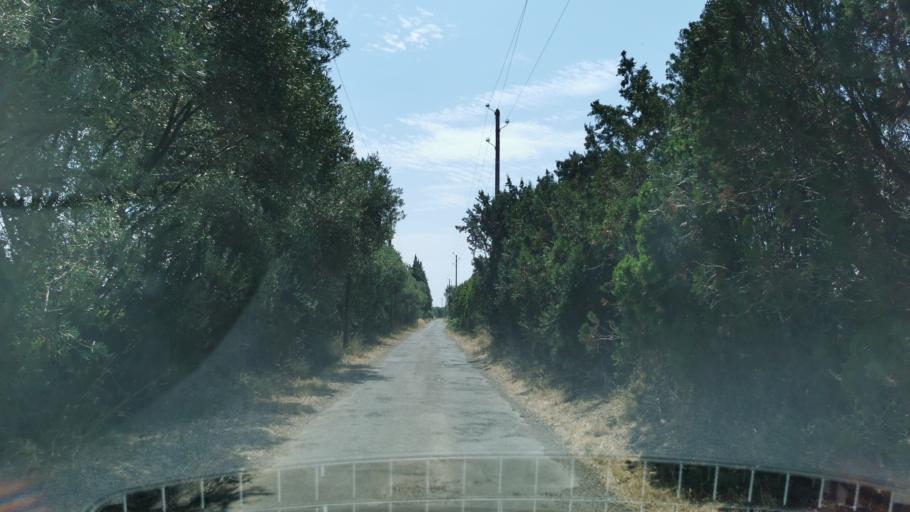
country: FR
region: Languedoc-Roussillon
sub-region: Departement de l'Aude
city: Bize-Minervois
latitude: 43.2945
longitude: 2.8825
